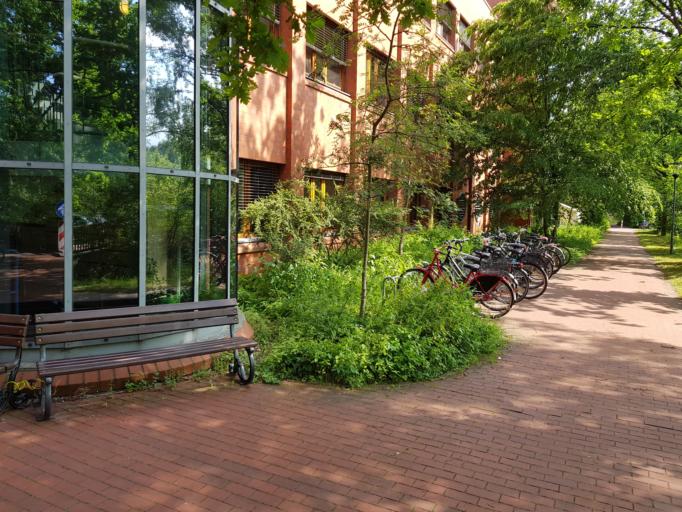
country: DE
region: Lower Saxony
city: Oldenburg
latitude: 53.1526
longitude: 8.1670
